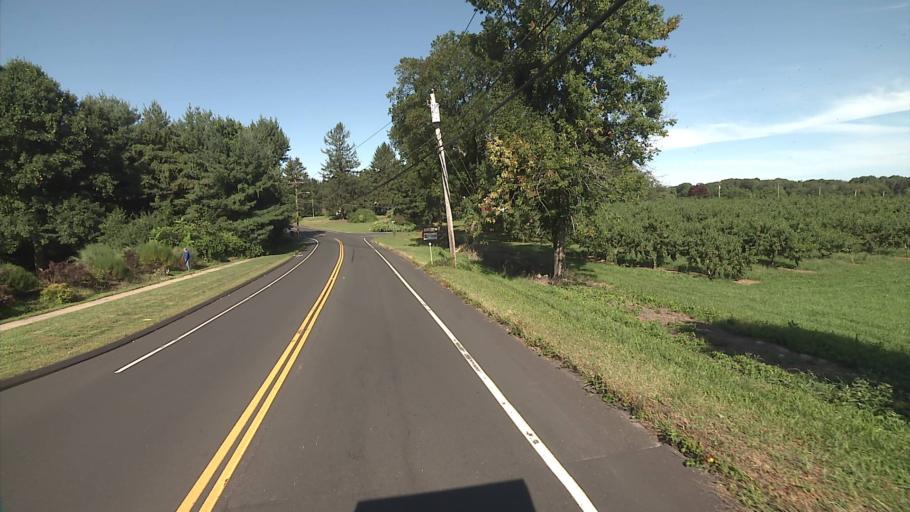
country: US
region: Connecticut
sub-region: New Haven County
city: Cheshire Village
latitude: 41.5008
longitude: -72.8851
